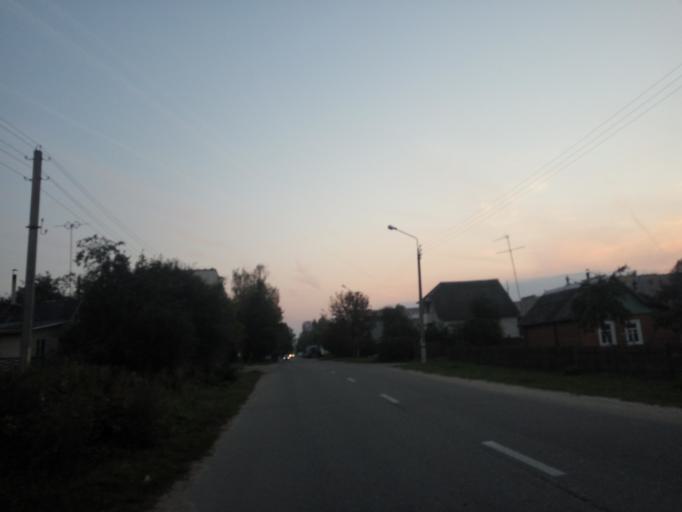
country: BY
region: Vitebsk
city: Vitebsk
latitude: 55.2025
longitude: 30.2435
